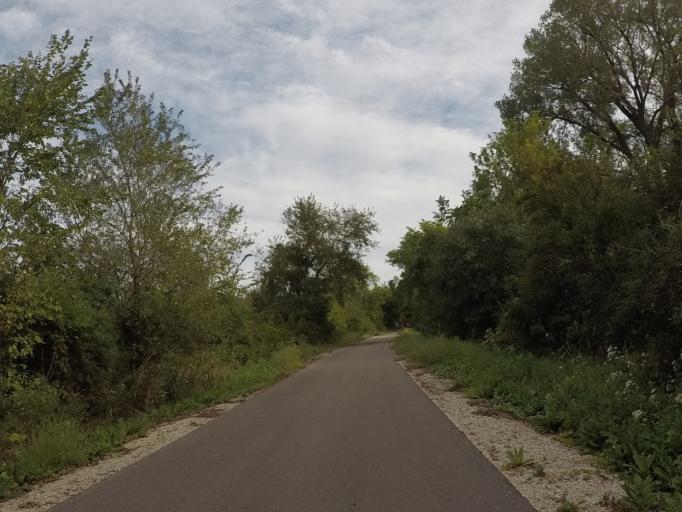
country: US
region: Wisconsin
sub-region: Sauk County
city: Prairie du Sac
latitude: 43.3346
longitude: -89.7497
